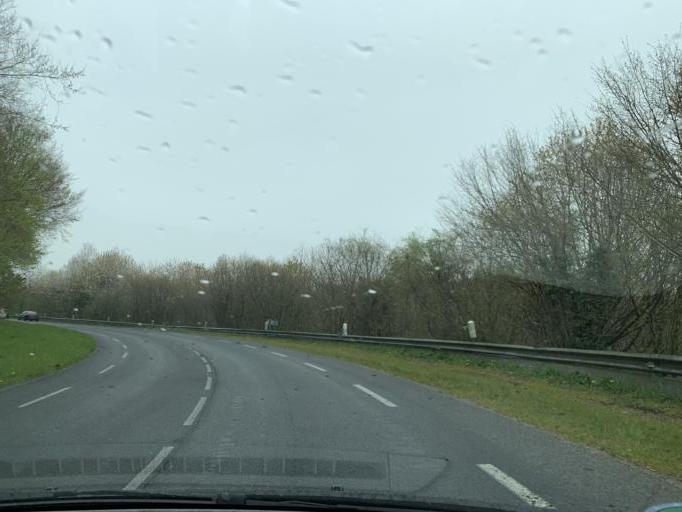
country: FR
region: Haute-Normandie
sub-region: Departement de la Seine-Maritime
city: Cany-Barville
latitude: 49.7831
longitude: 0.6524
